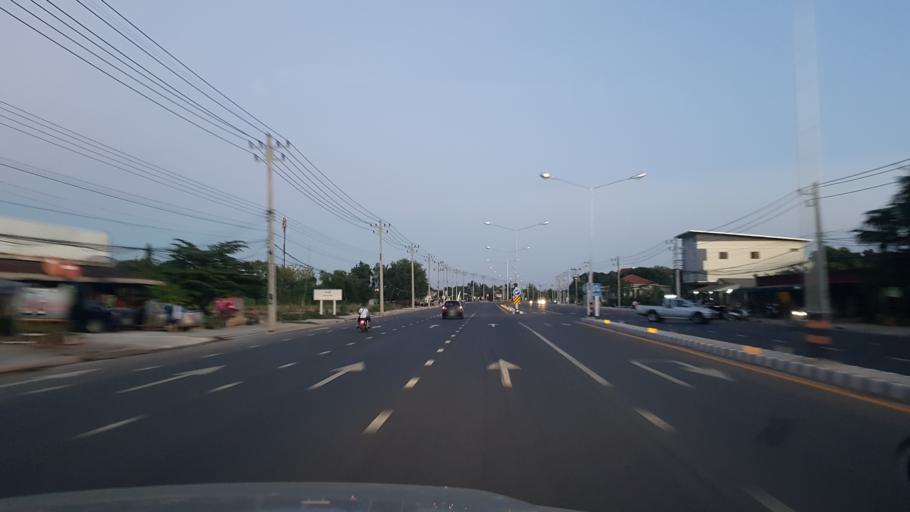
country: TH
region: Chaiyaphum
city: Phu Khiao
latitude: 16.3623
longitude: 102.1449
